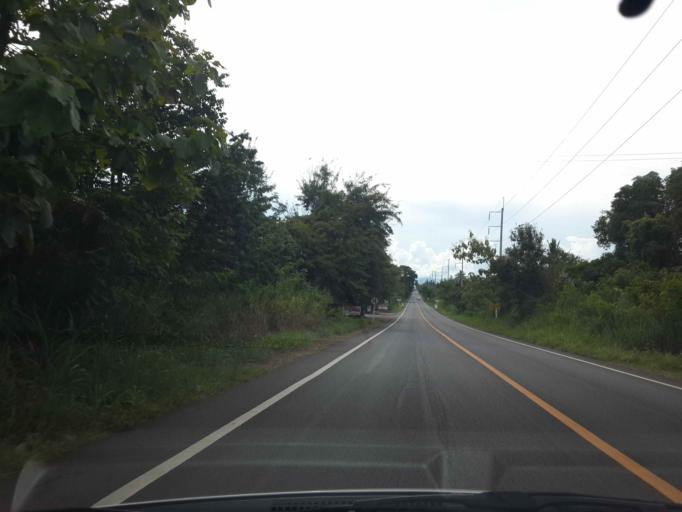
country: TH
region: Ratchaburi
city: Suan Phueng
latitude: 13.5479
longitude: 99.4650
